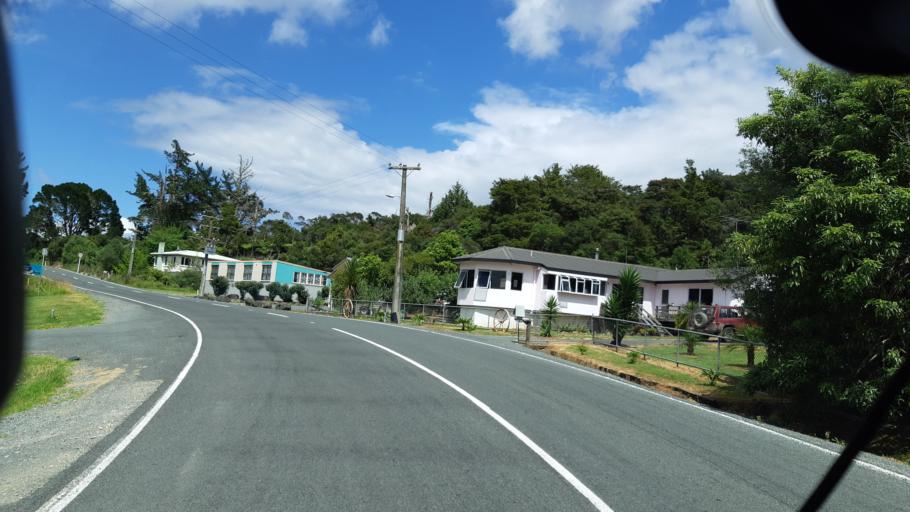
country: NZ
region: Northland
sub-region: Far North District
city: Taipa
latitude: -35.2369
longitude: 173.5439
